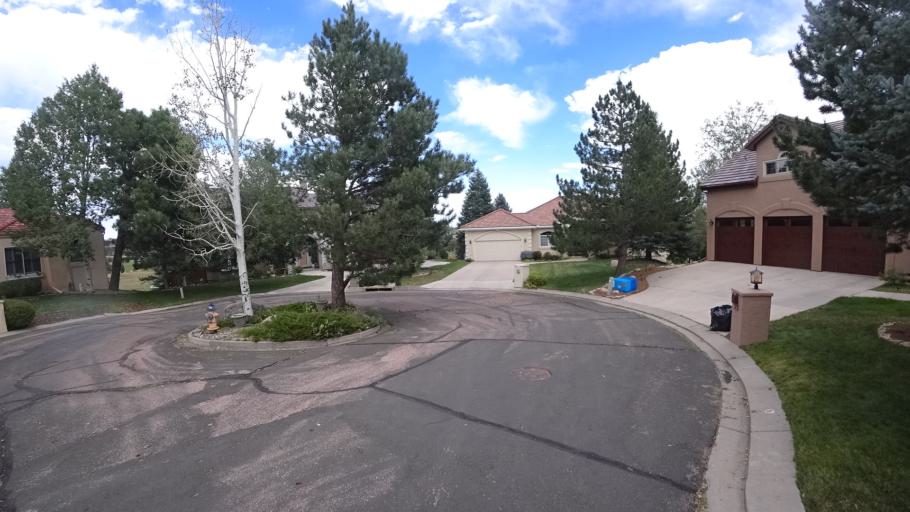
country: US
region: Colorado
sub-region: El Paso County
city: Stratmoor
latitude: 38.7749
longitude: -104.8260
